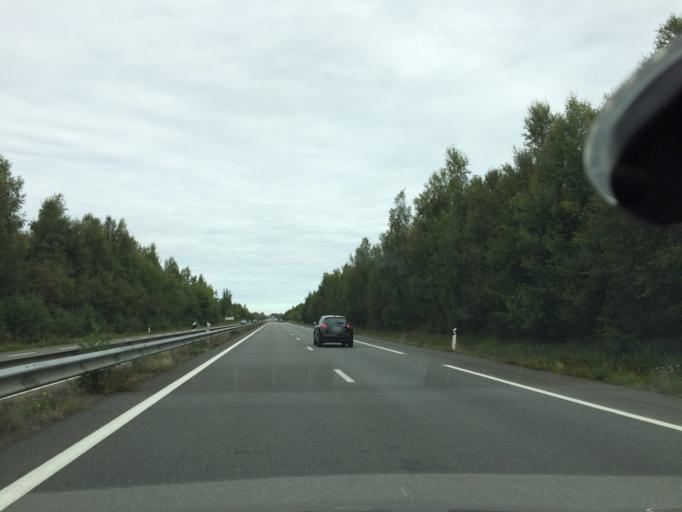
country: FR
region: Brittany
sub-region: Departement d'Ille-et-Vilaine
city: Saint-Domineuc
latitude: 48.3754
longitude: -1.8914
